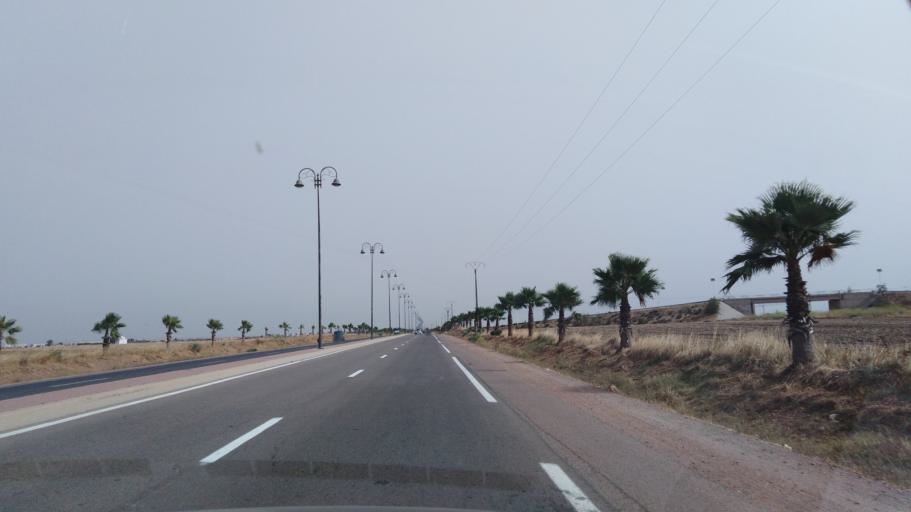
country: MA
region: Chaouia-Ouardigha
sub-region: Settat Province
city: Berrechid
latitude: 33.3070
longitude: -7.6016
